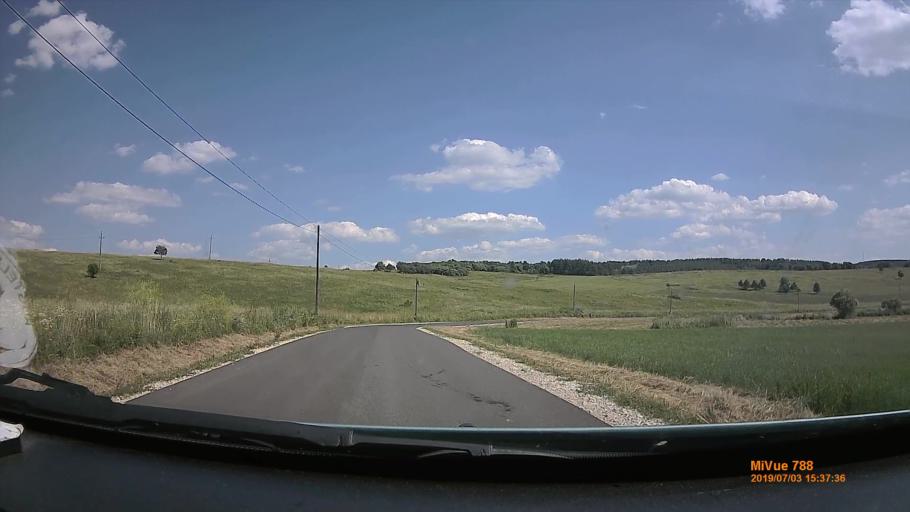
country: HU
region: Heves
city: Szilvasvarad
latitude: 48.1764
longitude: 20.3995
